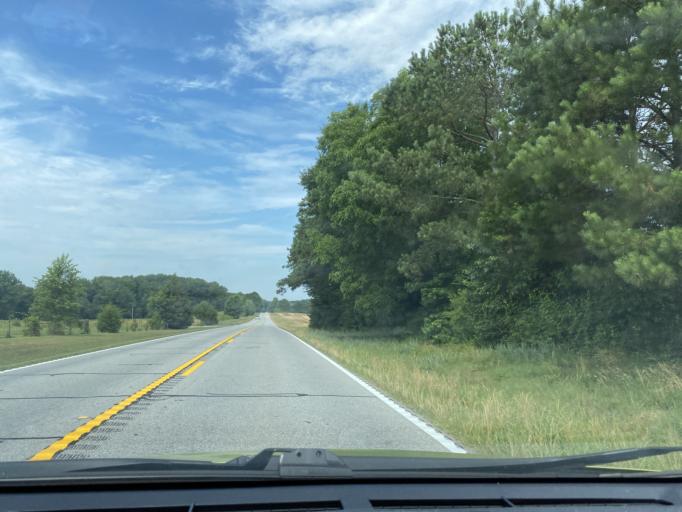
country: US
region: Georgia
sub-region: Coweta County
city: Senoia
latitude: 33.3025
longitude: -84.6675
